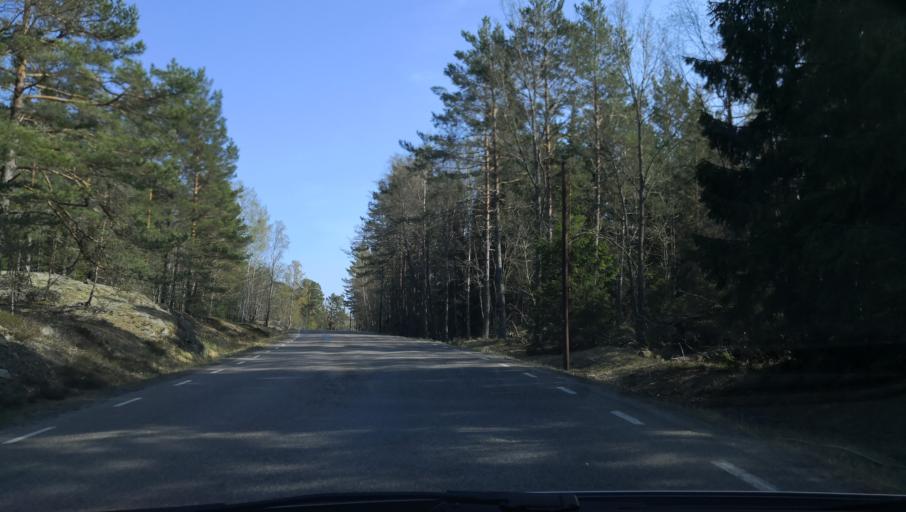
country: SE
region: Stockholm
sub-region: Varmdo Kommun
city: Hemmesta
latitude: 59.3113
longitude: 18.5787
